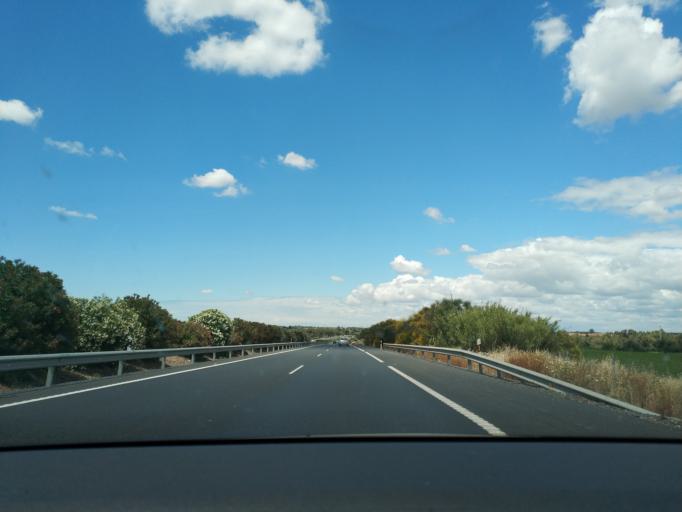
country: ES
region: Andalusia
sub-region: Provincia de Huelva
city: Bonares
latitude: 37.3410
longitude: -6.6990
